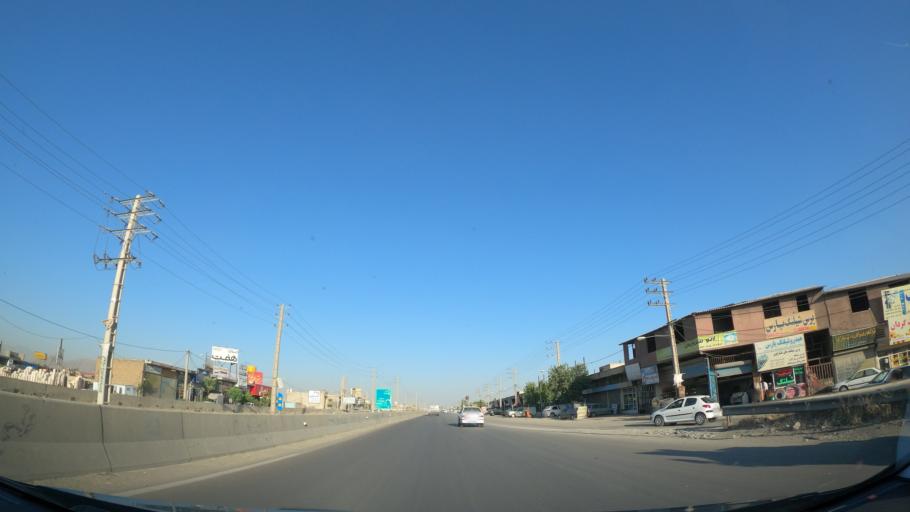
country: IR
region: Alborz
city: Hashtgerd
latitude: 35.9171
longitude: 50.7545
